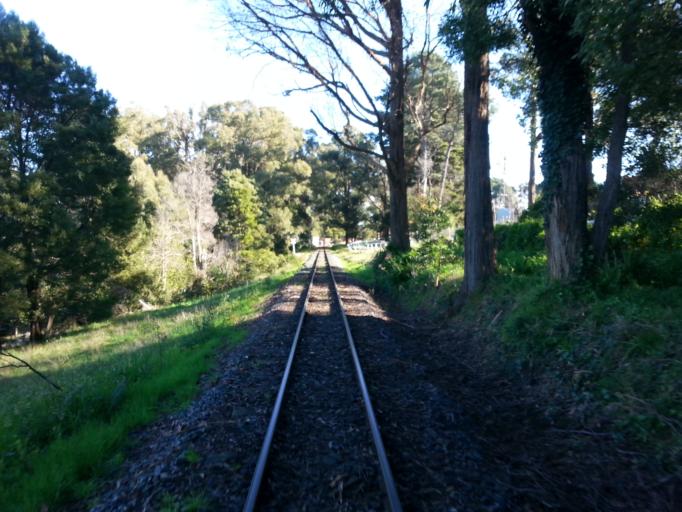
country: AU
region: Victoria
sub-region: Cardinia
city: Emerald
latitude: -37.9343
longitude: 145.4431
